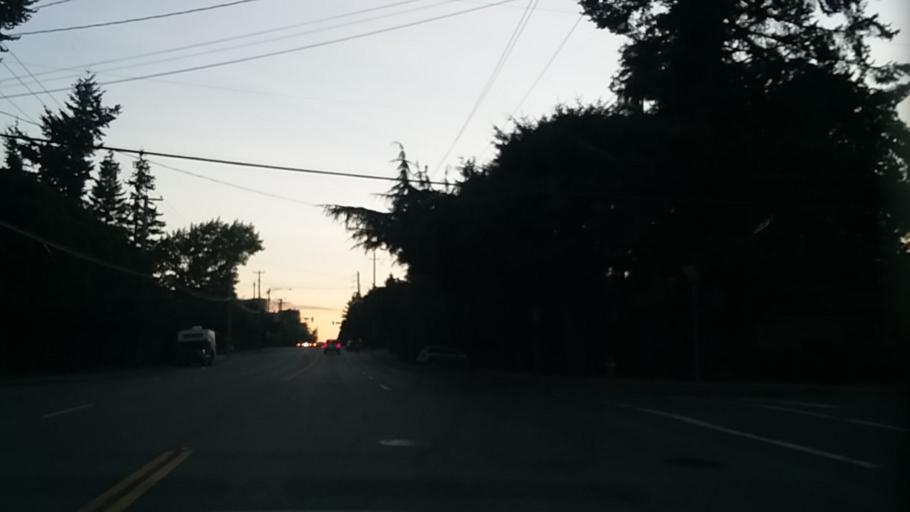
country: CA
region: British Columbia
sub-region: Greater Vancouver Regional District
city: White Rock
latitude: 49.0311
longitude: -122.7871
